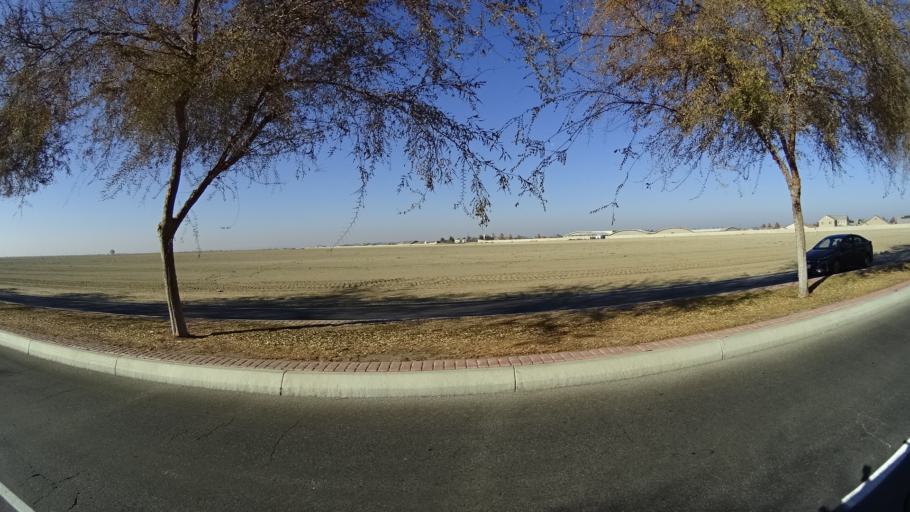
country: US
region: California
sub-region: Kern County
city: Rosedale
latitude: 35.3362
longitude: -119.1455
